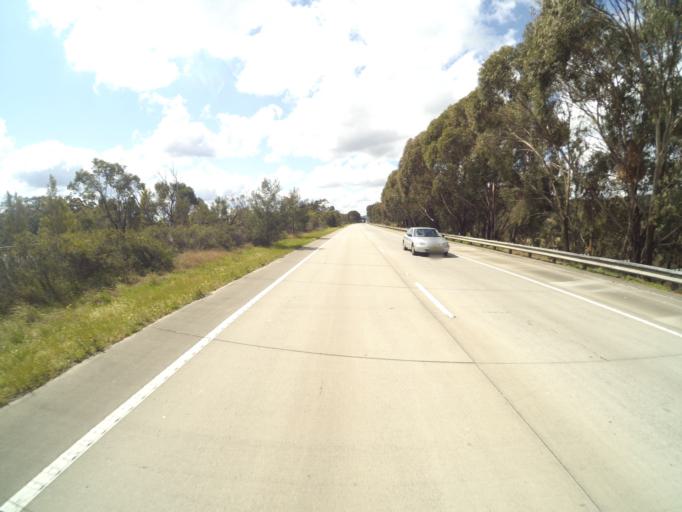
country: AU
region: New South Wales
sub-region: Wingecarribee
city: Bowral
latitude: -34.4467
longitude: 150.3845
